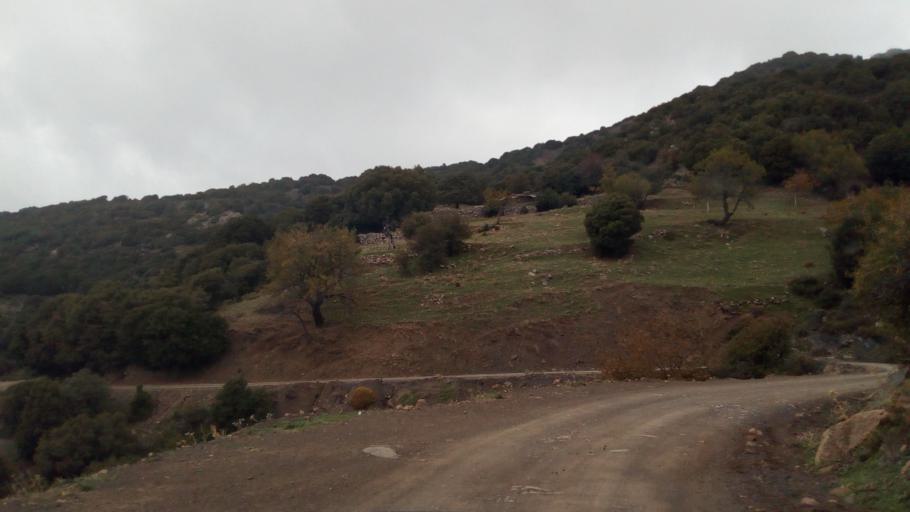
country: GR
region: West Greece
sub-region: Nomos Achaias
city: Selianitika
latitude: 38.4160
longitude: 22.0949
